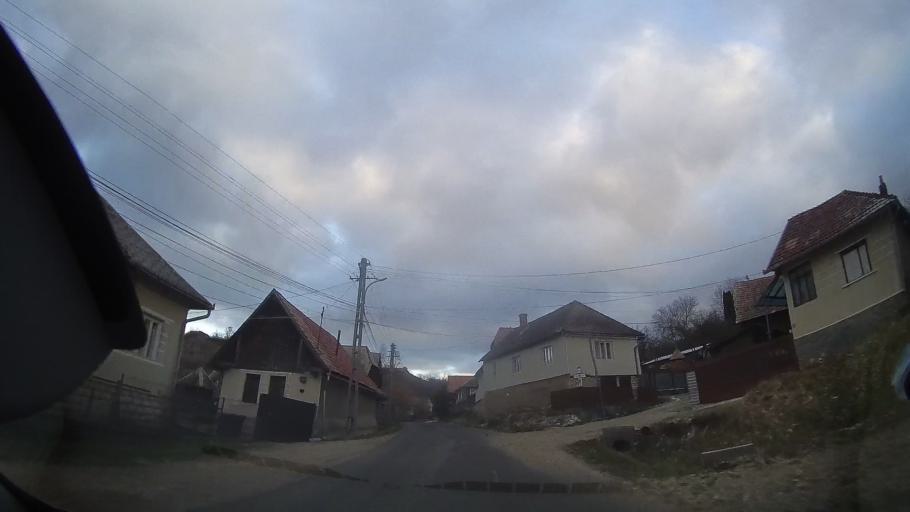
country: RO
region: Cluj
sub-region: Comuna Calatele
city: Calatele
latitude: 46.7807
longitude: 23.0366
